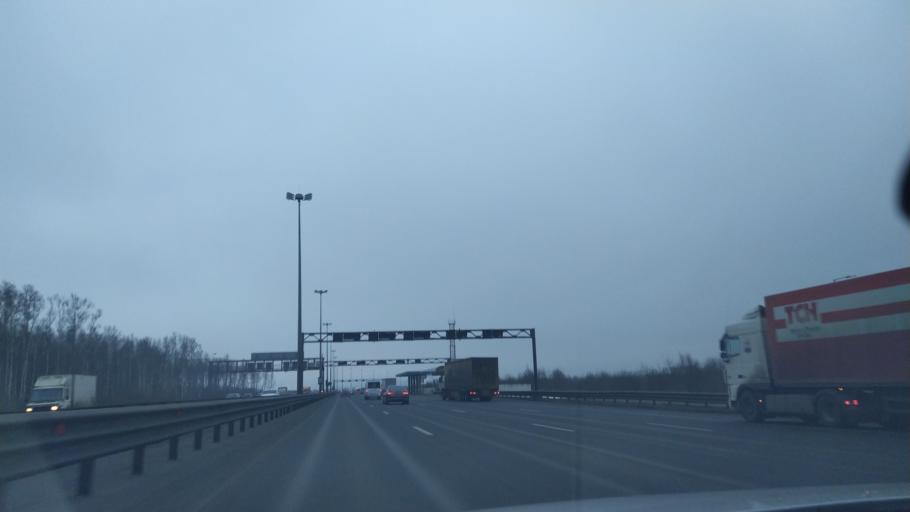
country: RU
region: Leningrad
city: Rybatskoye
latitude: 59.8784
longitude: 30.5292
